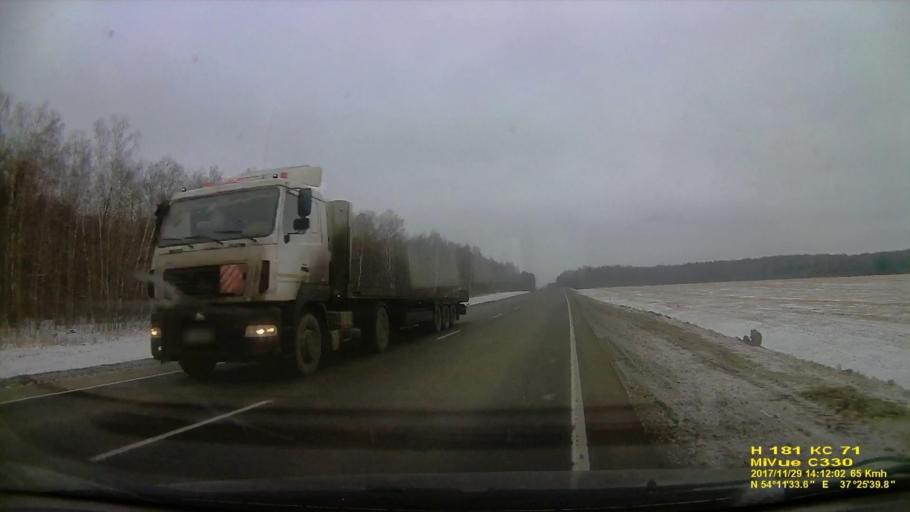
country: RU
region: Tula
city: Barsuki
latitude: 54.1926
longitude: 37.4279
